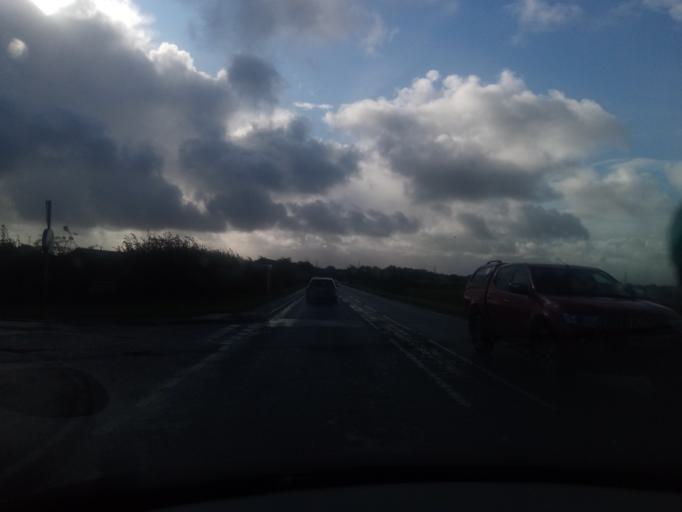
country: GB
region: England
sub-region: Cumbria
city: Carlisle
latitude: 54.9532
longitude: -2.9436
